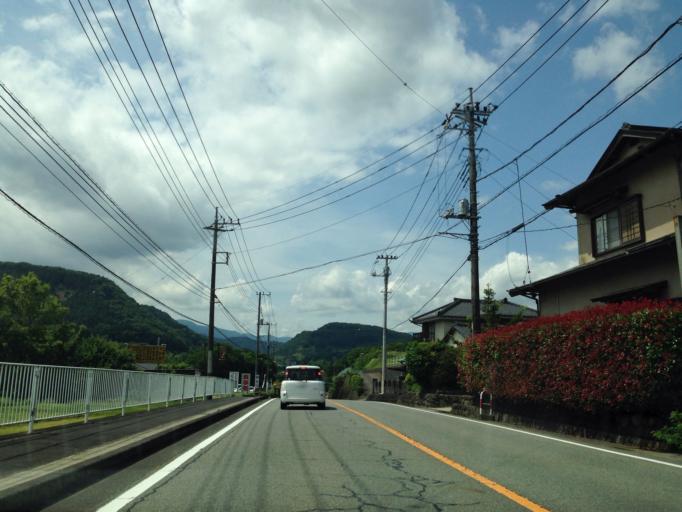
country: JP
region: Shizuoka
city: Ito
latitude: 34.9508
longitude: 138.9355
